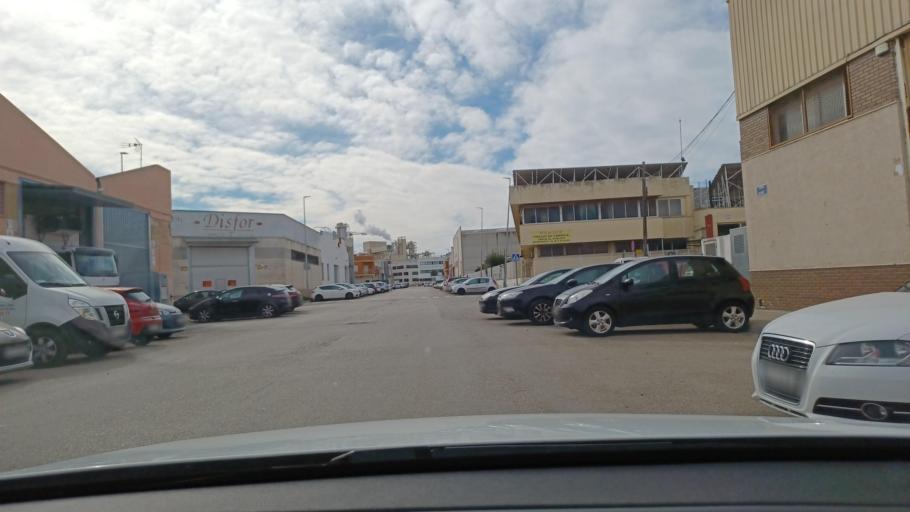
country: ES
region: Valencia
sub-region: Provincia de Valencia
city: Benifaio
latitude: 39.2869
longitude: -0.4322
